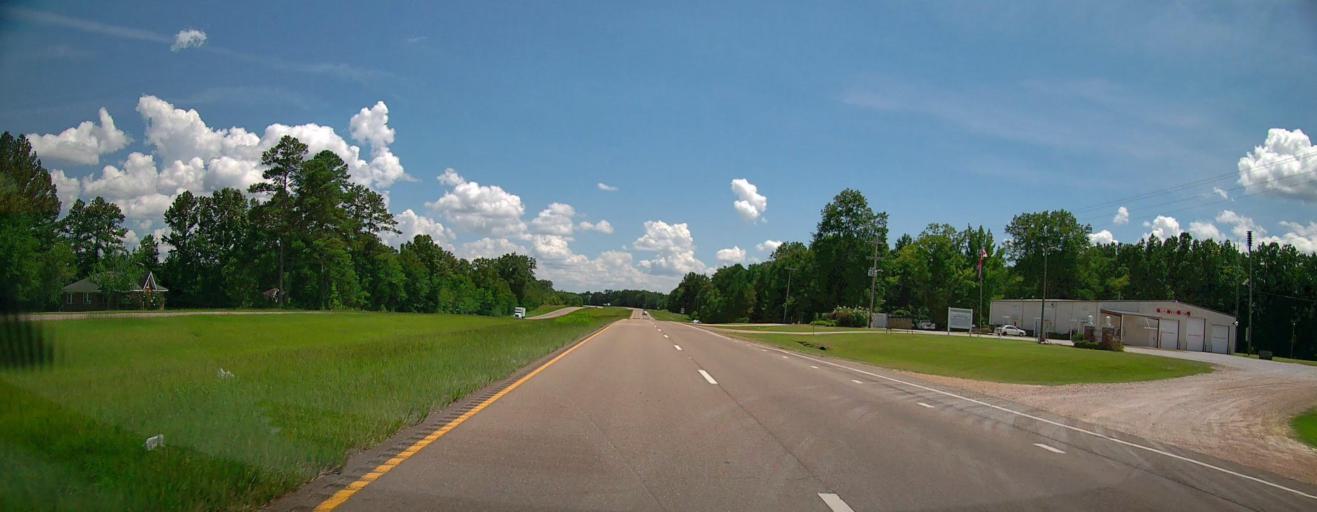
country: US
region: Mississippi
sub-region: Lee County
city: Nettleton
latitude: 33.9722
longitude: -88.6139
